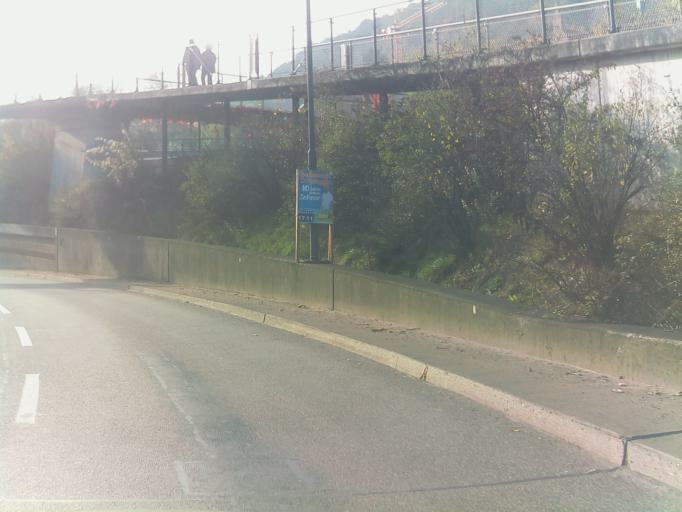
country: DE
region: Baden-Wuerttemberg
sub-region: Karlsruhe Region
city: Mosbach
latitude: 49.3545
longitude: 9.1448
